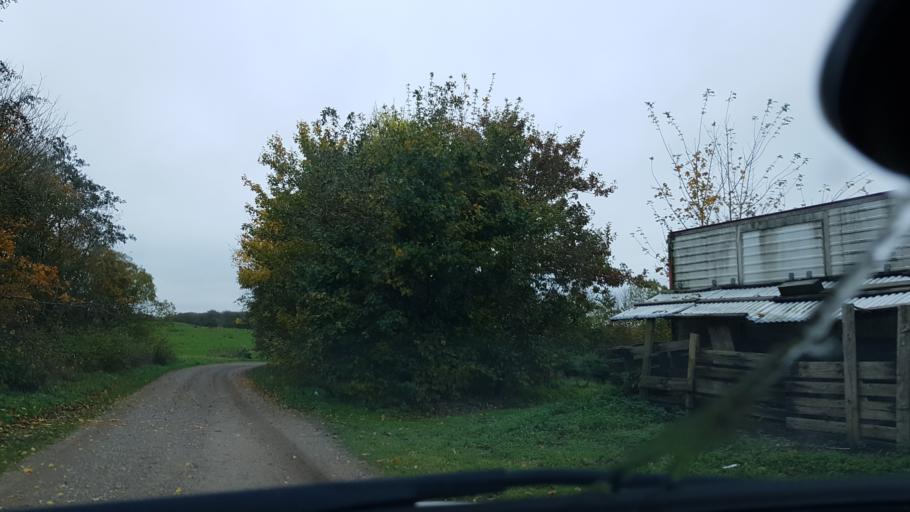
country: DK
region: South Denmark
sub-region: Esbjerg Kommune
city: Ribe
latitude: 55.2798
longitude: 8.8543
